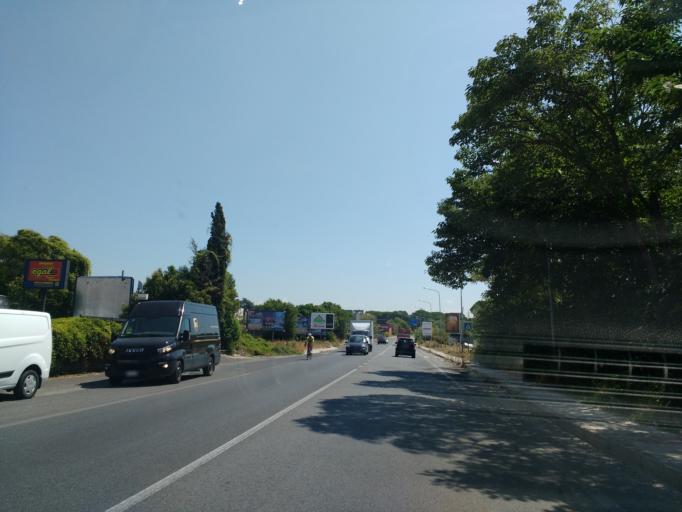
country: IT
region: Latium
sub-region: Citta metropolitana di Roma Capitale
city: Albuccione
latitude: 41.9520
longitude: 12.6927
